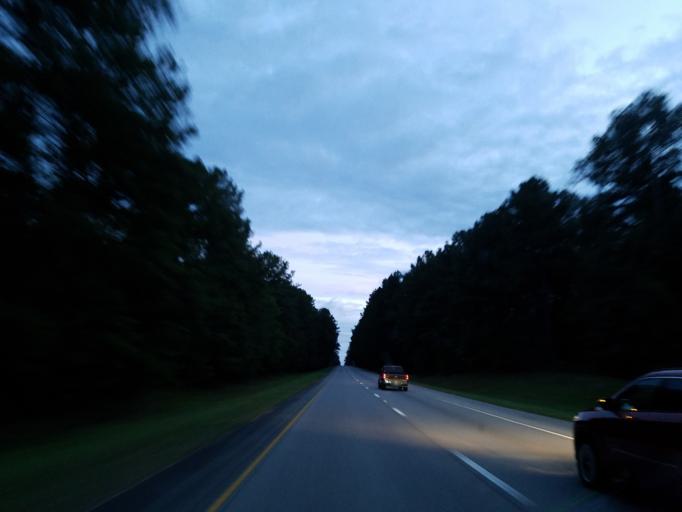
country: US
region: Mississippi
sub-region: Clarke County
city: Stonewall
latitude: 32.1720
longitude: -88.8670
